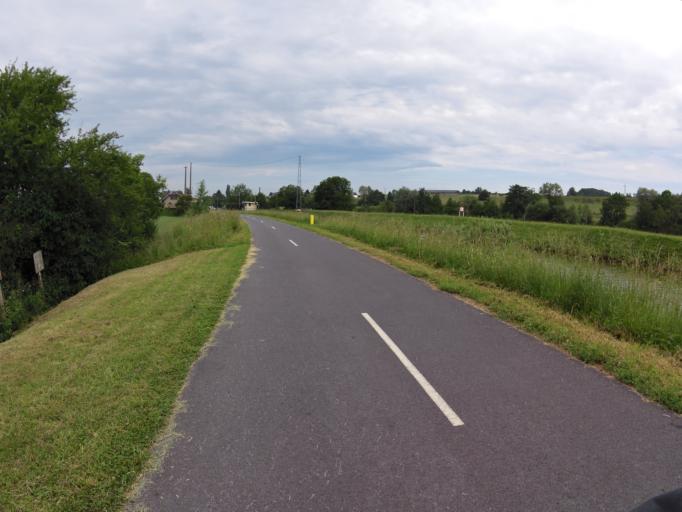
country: FR
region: Champagne-Ardenne
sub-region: Departement des Ardennes
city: Dom-le-Mesnil
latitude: 49.6948
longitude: 4.8123
